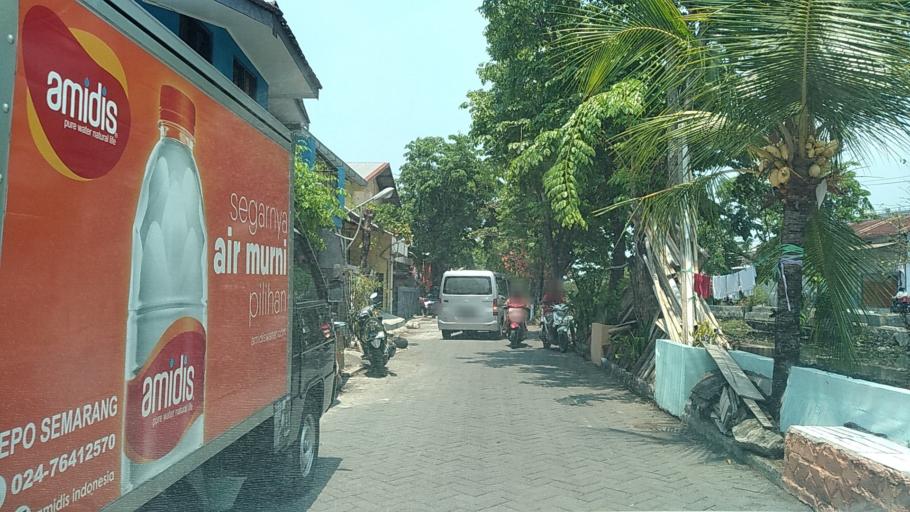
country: ID
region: Central Java
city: Semarang
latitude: -6.9691
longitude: 110.4390
